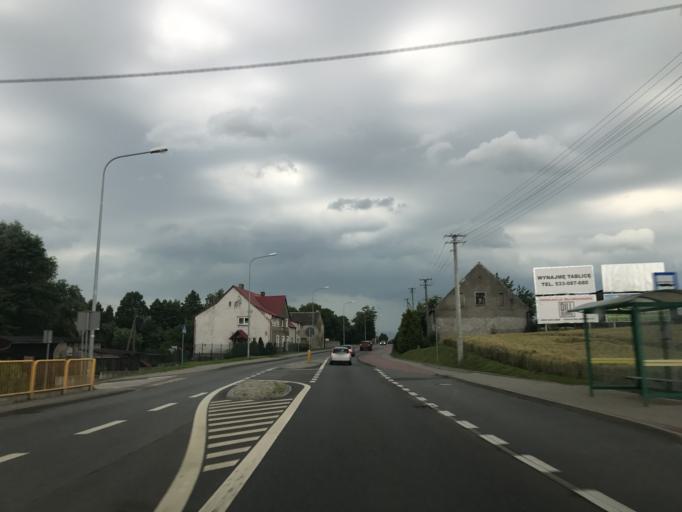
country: PL
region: Kujawsko-Pomorskie
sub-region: Powiat tucholski
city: Kesowo
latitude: 53.6461
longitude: 17.7100
